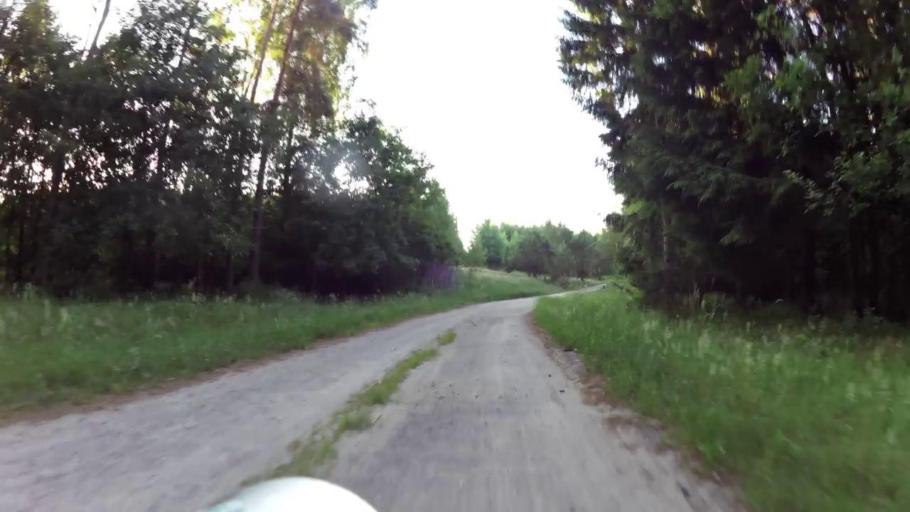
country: PL
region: West Pomeranian Voivodeship
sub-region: Powiat szczecinecki
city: Szczecinek
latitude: 53.8364
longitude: 16.6882
